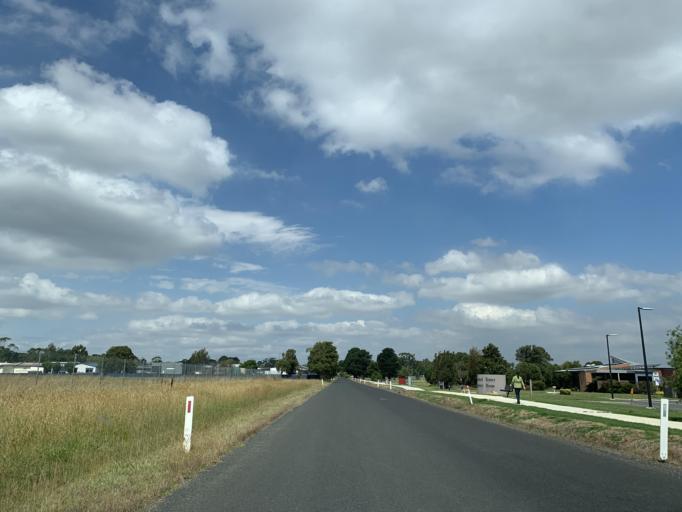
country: AU
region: Victoria
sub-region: Latrobe
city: Traralgon
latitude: -38.2150
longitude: 146.4713
